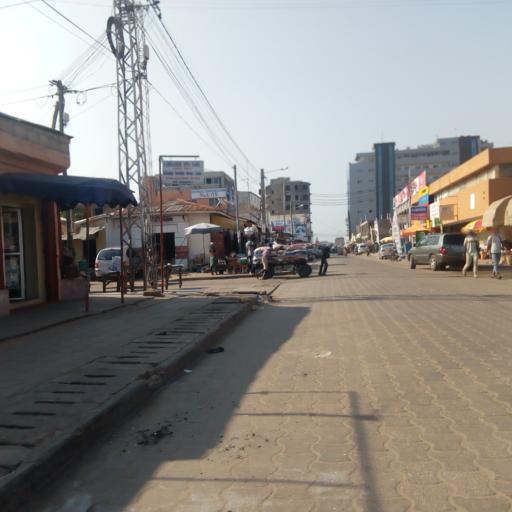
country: TG
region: Maritime
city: Lome
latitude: 6.1340
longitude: 1.2286
